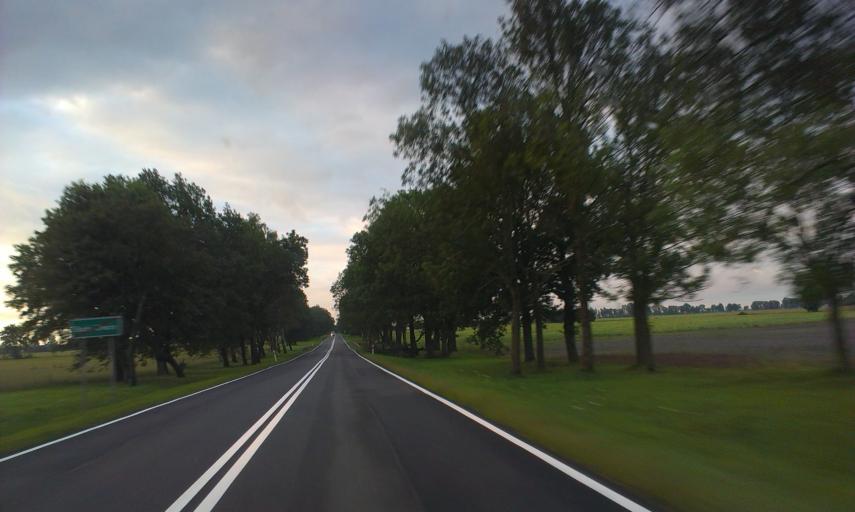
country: PL
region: Greater Poland Voivodeship
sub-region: Powiat zlotowski
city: Okonek
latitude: 53.6168
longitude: 16.7870
